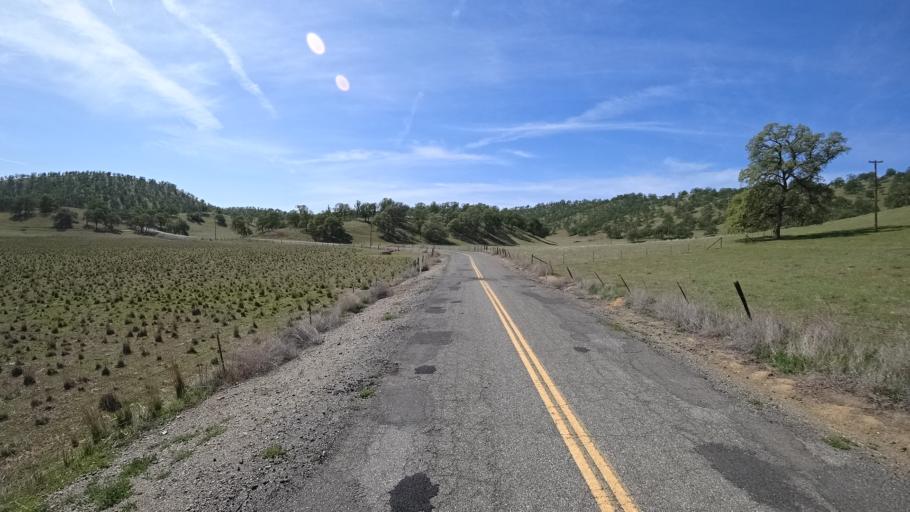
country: US
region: California
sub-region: Glenn County
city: Willows
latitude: 39.5462
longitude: -122.4302
